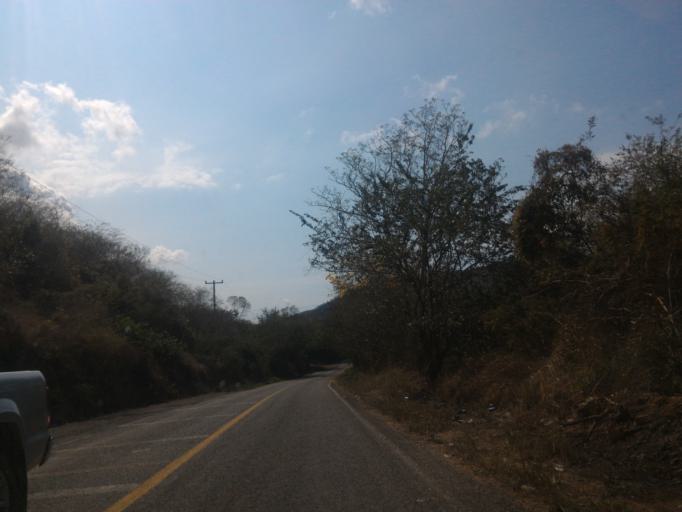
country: MX
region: Michoacan
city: Coahuayana Viejo
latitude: 18.4683
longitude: -103.5444
